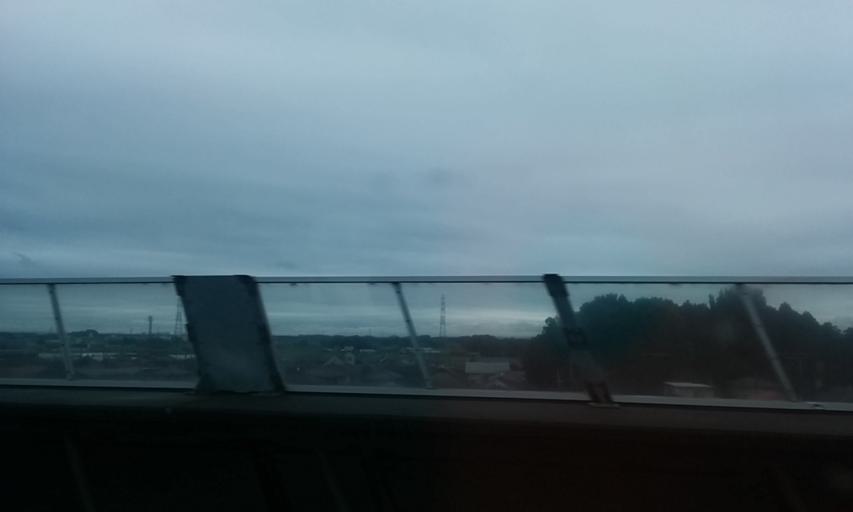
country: JP
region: Tochigi
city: Kaminokawa
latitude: 36.4799
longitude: 139.8746
